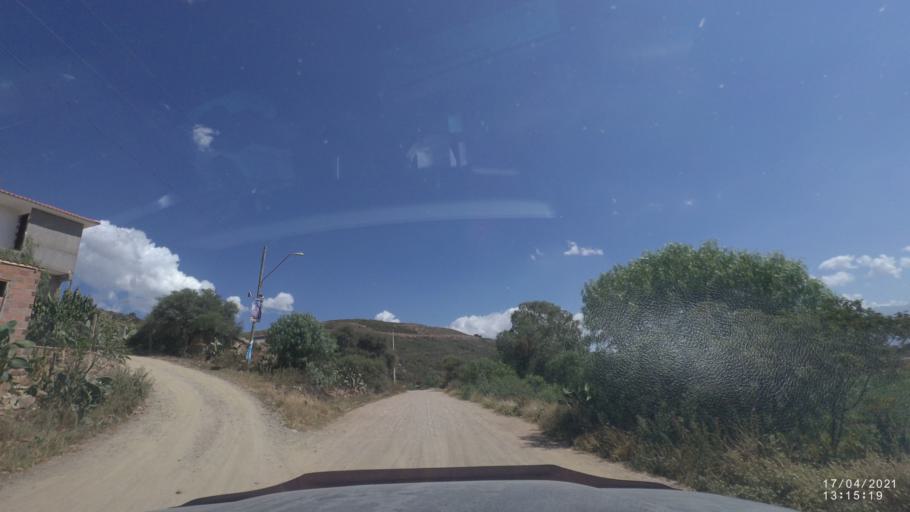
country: BO
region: Cochabamba
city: Cochabamba
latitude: -17.4168
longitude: -66.2306
